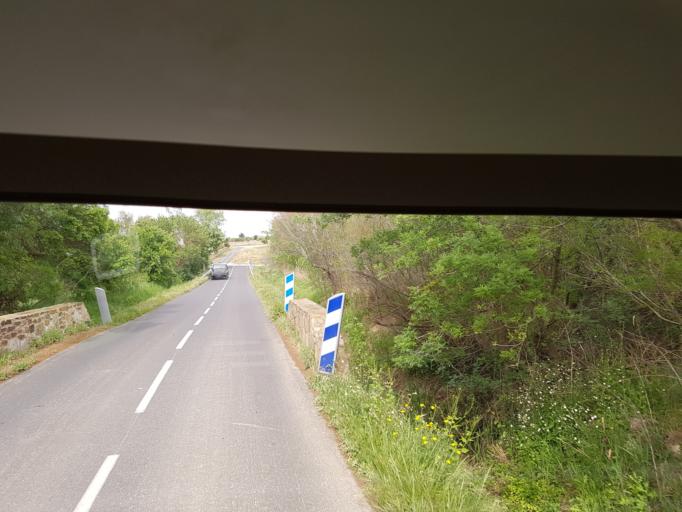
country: FR
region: Languedoc-Roussillon
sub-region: Departement de l'Herault
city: Lespignan
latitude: 43.2565
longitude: 3.1591
